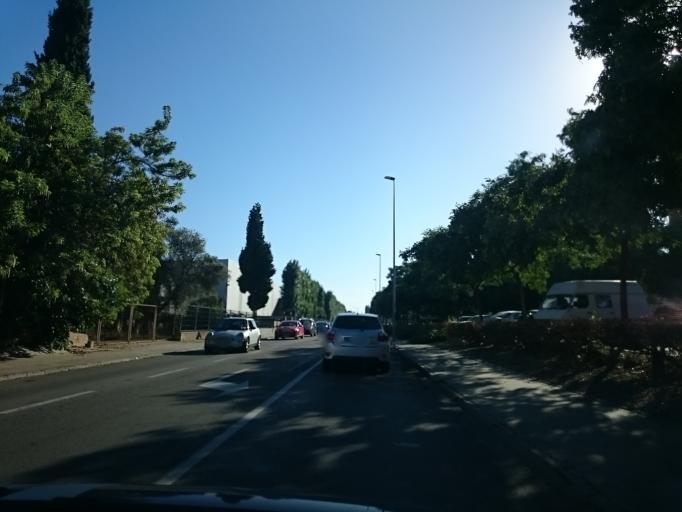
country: ES
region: Catalonia
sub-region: Provincia de Barcelona
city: Viladecans
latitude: 41.3106
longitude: 2.0156
